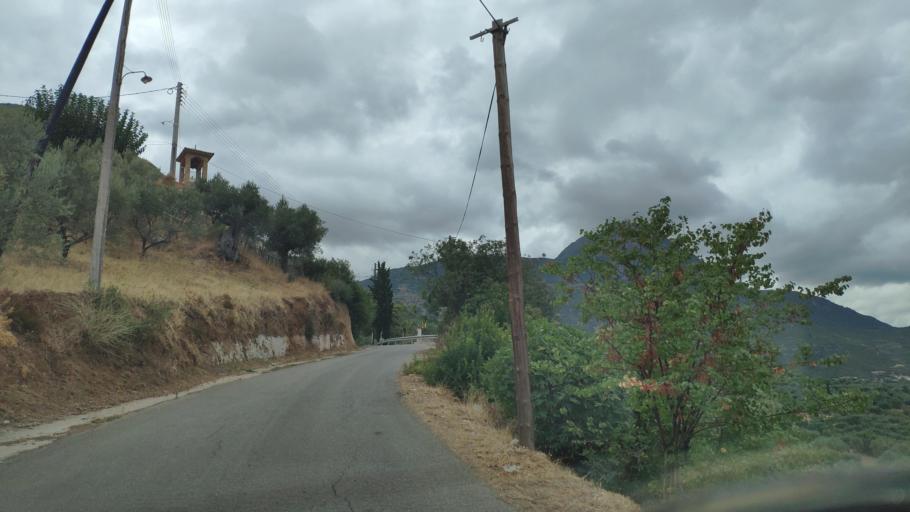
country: GR
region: West Greece
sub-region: Nomos Achaias
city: Temeni
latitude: 38.1770
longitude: 22.1440
